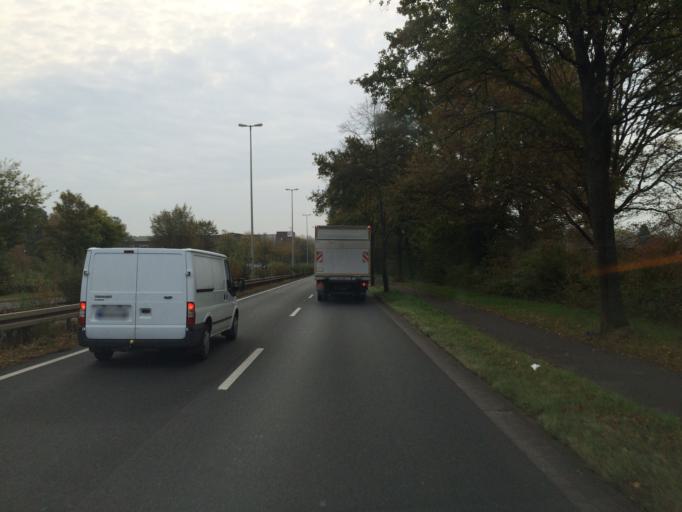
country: DE
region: Lower Saxony
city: Hannover
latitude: 52.3469
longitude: 9.7061
